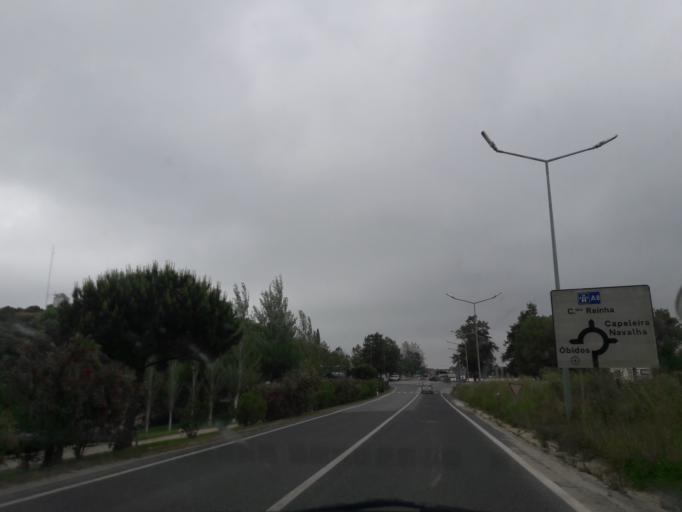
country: PT
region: Leiria
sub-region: Obidos
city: Obidos
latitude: 39.3557
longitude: -9.1585
